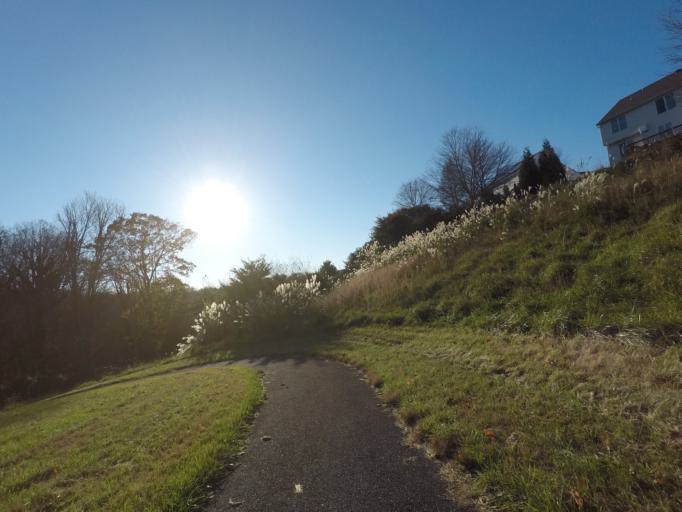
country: US
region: Maryland
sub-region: Howard County
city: Ellicott City
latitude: 39.2807
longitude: -76.7912
